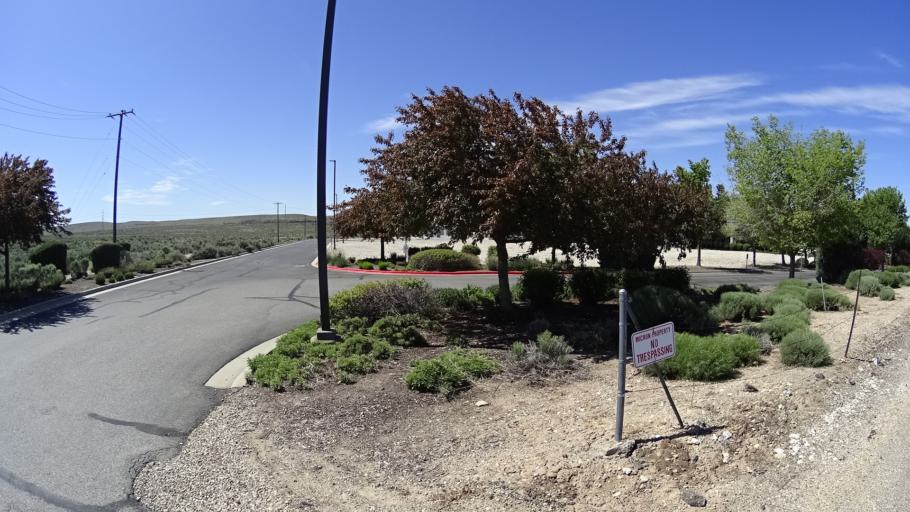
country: US
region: Idaho
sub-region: Ada County
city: Boise
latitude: 43.5311
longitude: -116.1345
